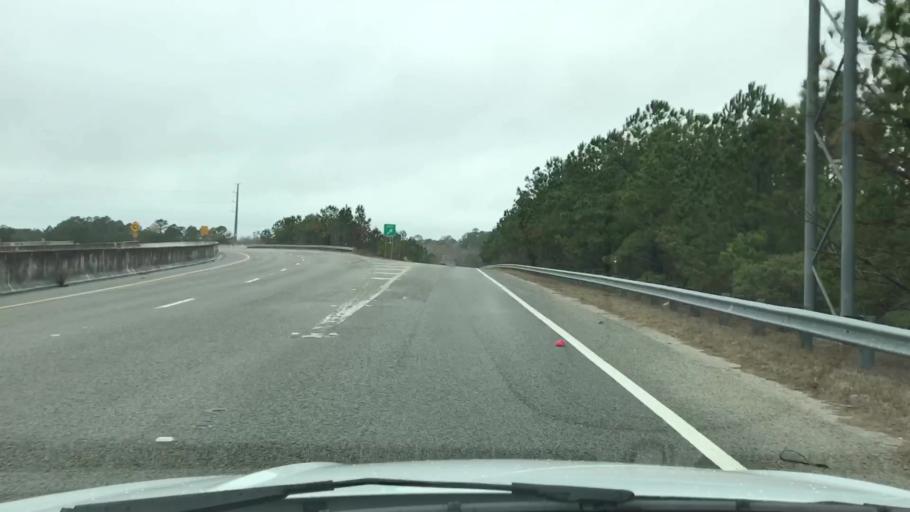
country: US
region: South Carolina
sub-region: Horry County
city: Forestbrook
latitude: 33.7417
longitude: -78.9500
